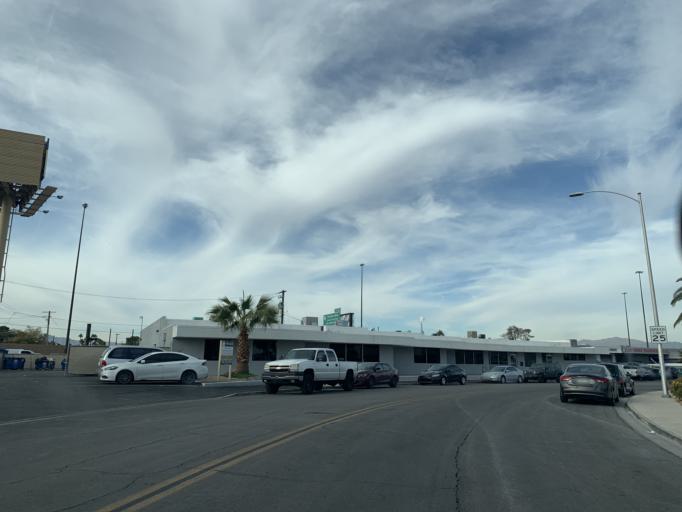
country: US
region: Nevada
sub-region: Clark County
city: Las Vegas
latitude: 36.1470
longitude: -115.1670
